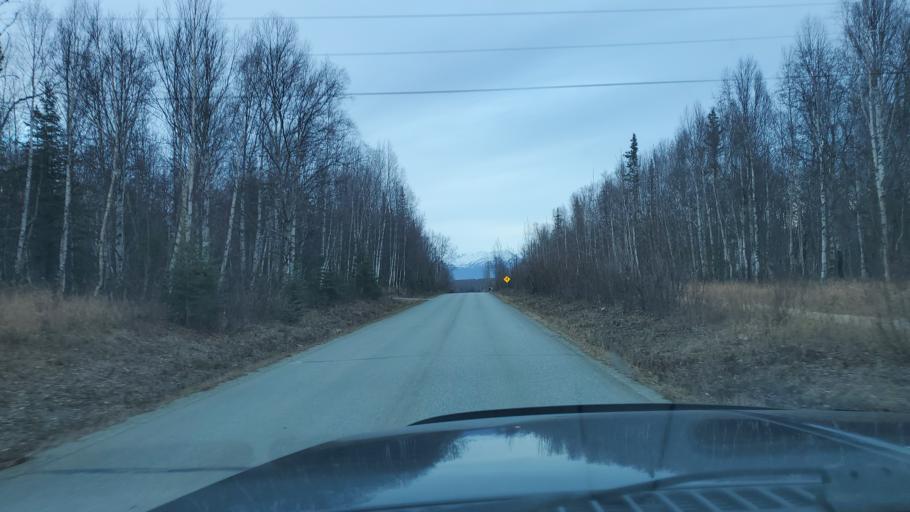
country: US
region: Alaska
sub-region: Matanuska-Susitna Borough
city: Lakes
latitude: 61.6572
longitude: -149.2988
